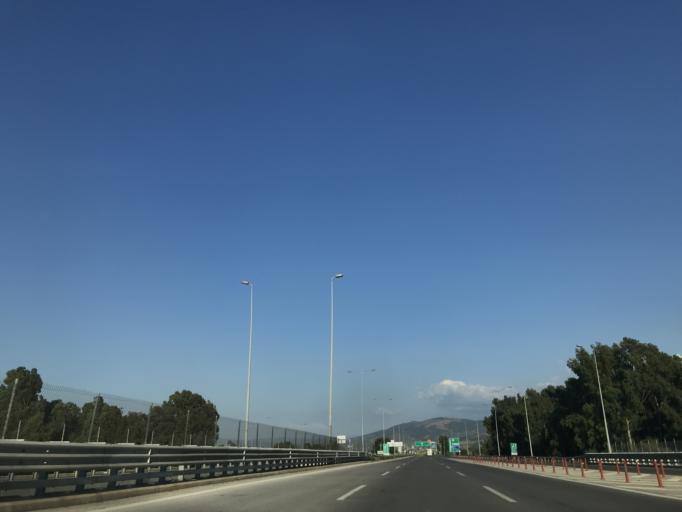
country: TR
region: Aydin
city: Aydin
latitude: 37.8190
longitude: 27.8465
